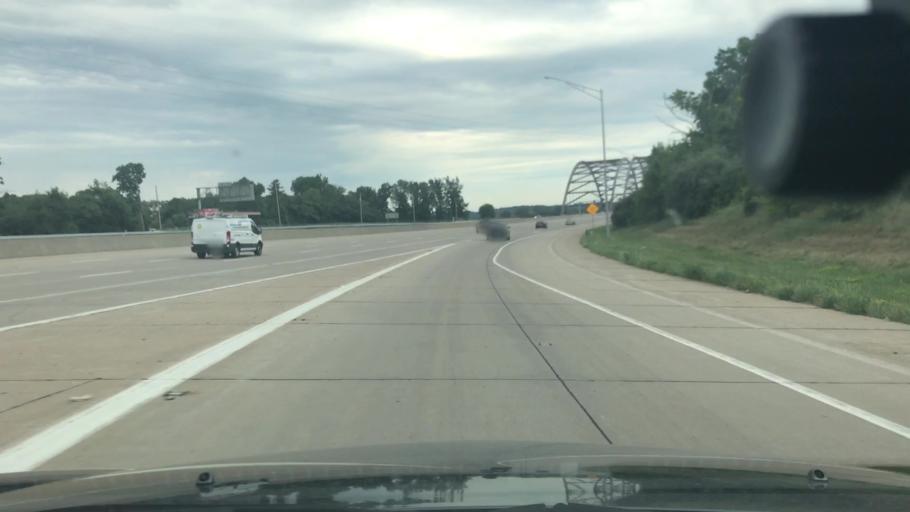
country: US
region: Missouri
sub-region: Saint Charles County
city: Saint Charles
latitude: 38.7414
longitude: -90.5268
